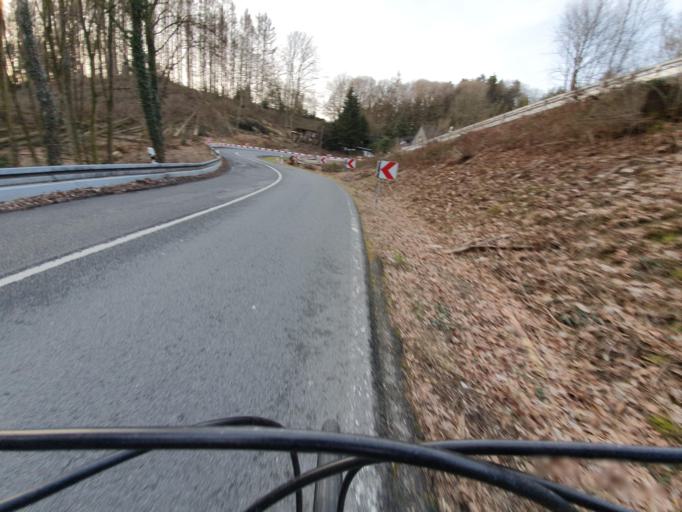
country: DE
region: North Rhine-Westphalia
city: Burscheid
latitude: 51.0870
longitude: 7.1611
